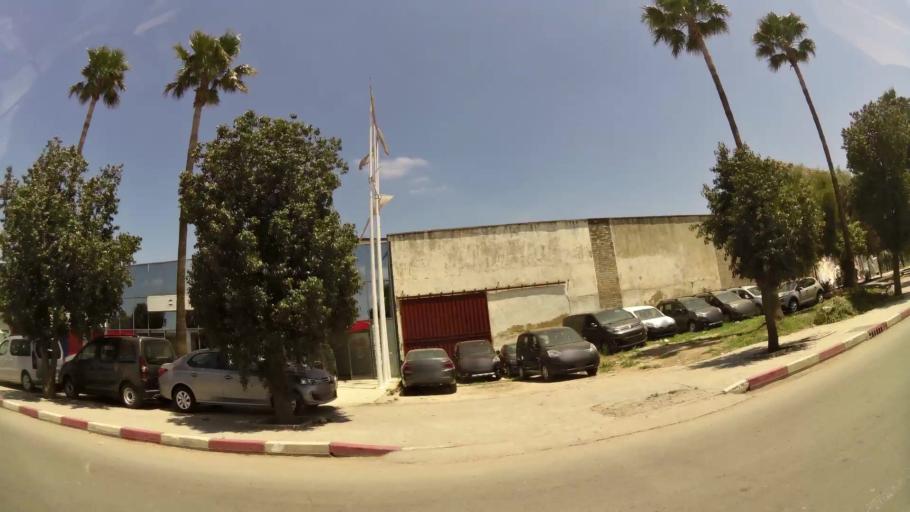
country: MA
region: Fes-Boulemane
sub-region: Fes
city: Fes
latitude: 34.0411
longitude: -5.0351
